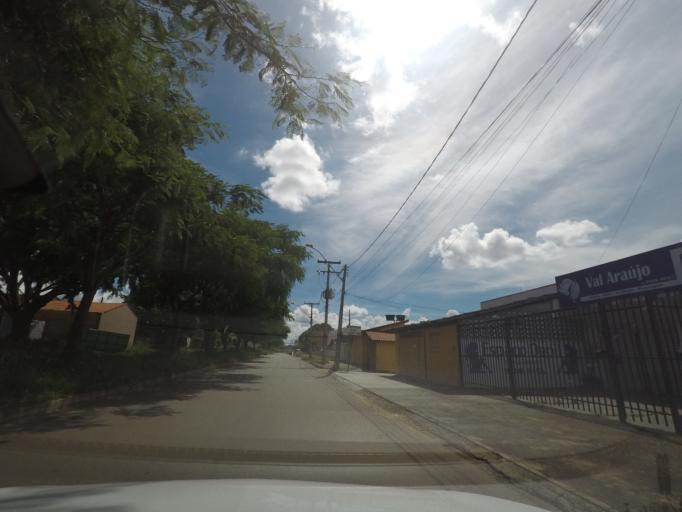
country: BR
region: Goias
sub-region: Goiania
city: Goiania
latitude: -16.7443
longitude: -49.3312
